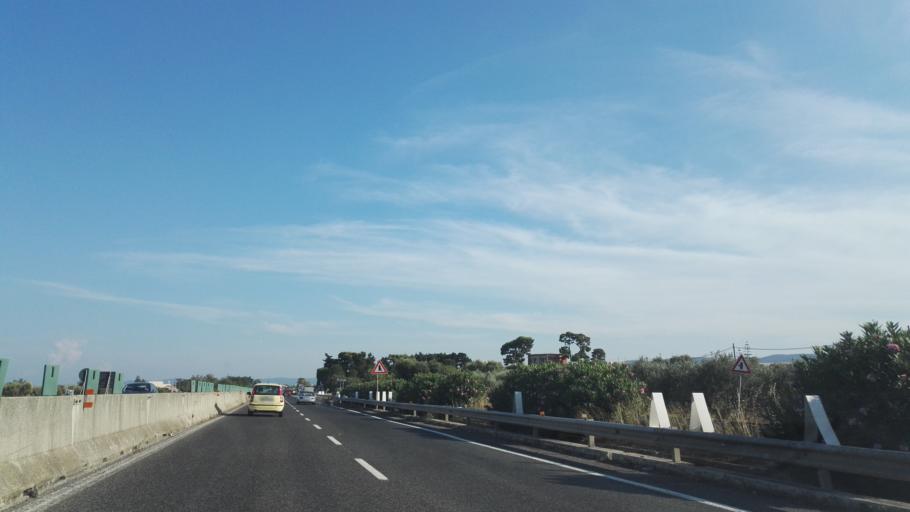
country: IT
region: Apulia
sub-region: Provincia di Bari
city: Monopoli
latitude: 40.9051
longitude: 17.3252
